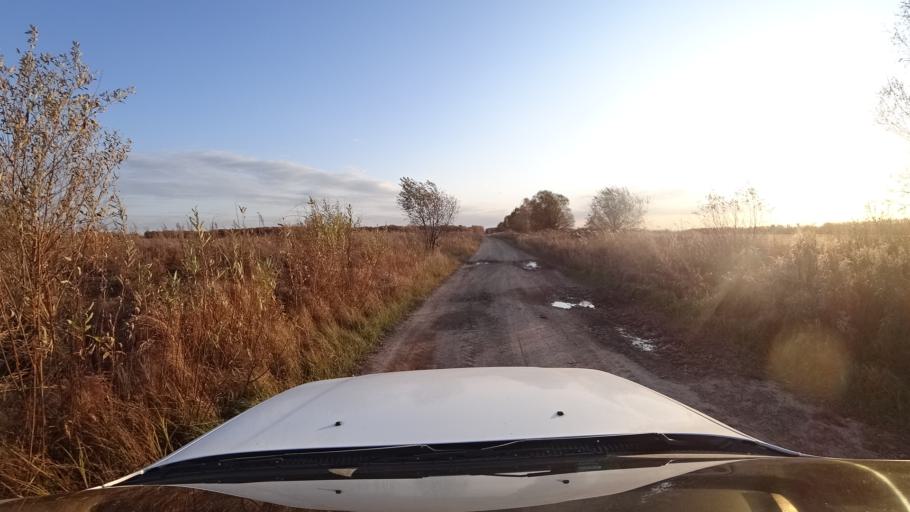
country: RU
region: Primorskiy
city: Lazo
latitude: 45.8111
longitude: 133.6083
